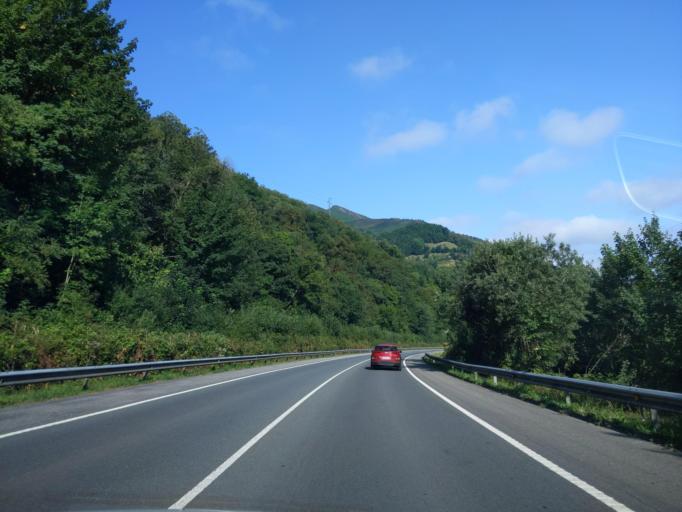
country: ES
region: Asturias
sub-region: Province of Asturias
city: Pola de Laviana
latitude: 43.2360
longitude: -5.5604
